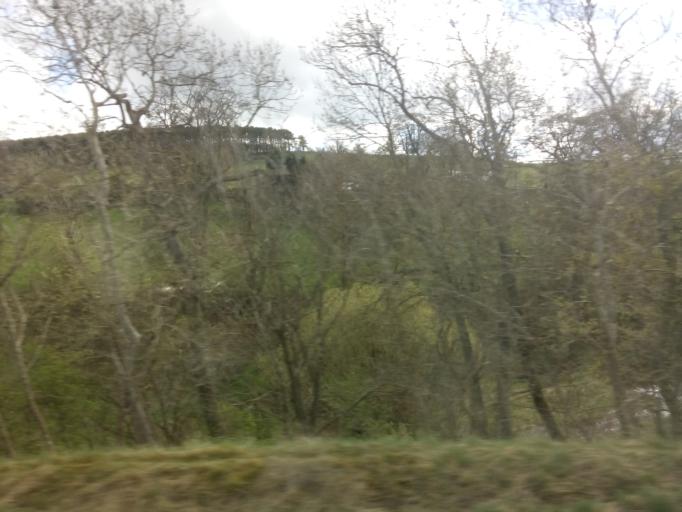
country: GB
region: Scotland
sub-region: The Scottish Borders
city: Chirnside
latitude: 55.8559
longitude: -2.2192
